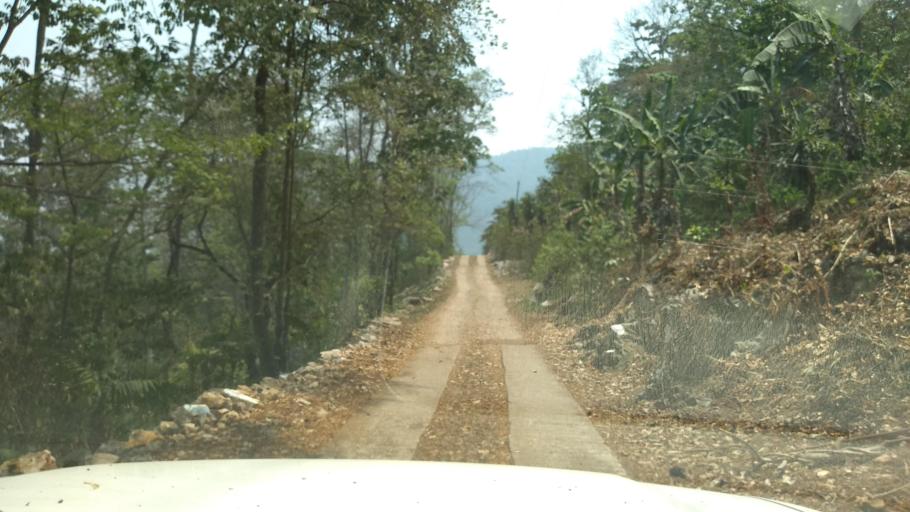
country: MX
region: Veracruz
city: Cosolapa
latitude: 18.5981
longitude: -96.7268
